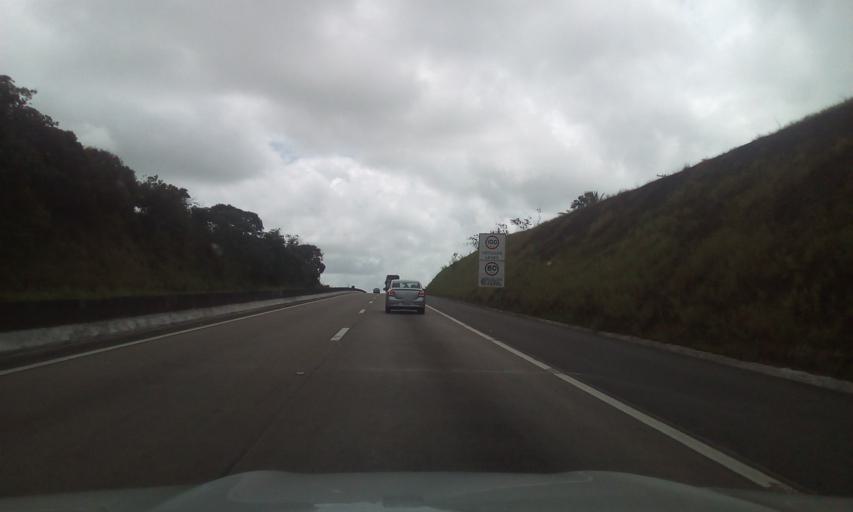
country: BR
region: Pernambuco
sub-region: Itapissuma
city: Itapissuma
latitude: -7.6807
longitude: -34.9257
